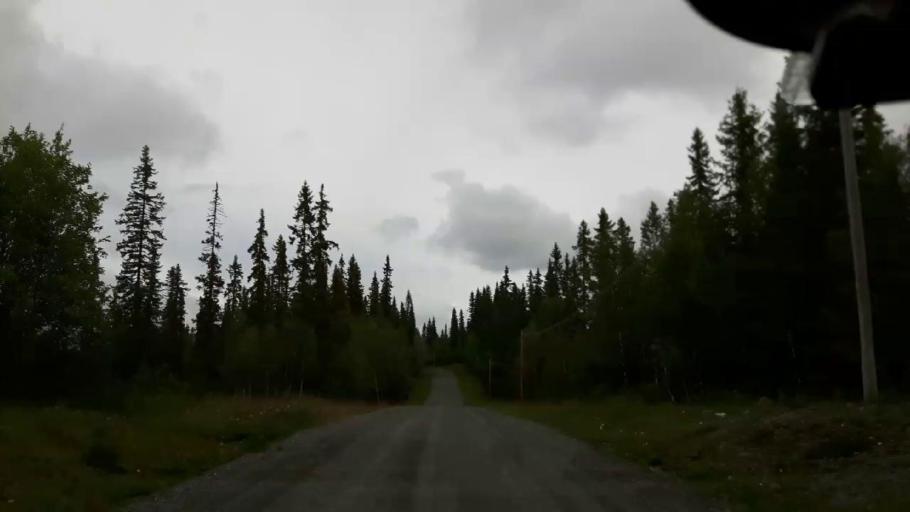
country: SE
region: Jaemtland
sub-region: Krokoms Kommun
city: Valla
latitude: 63.7161
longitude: 13.8593
